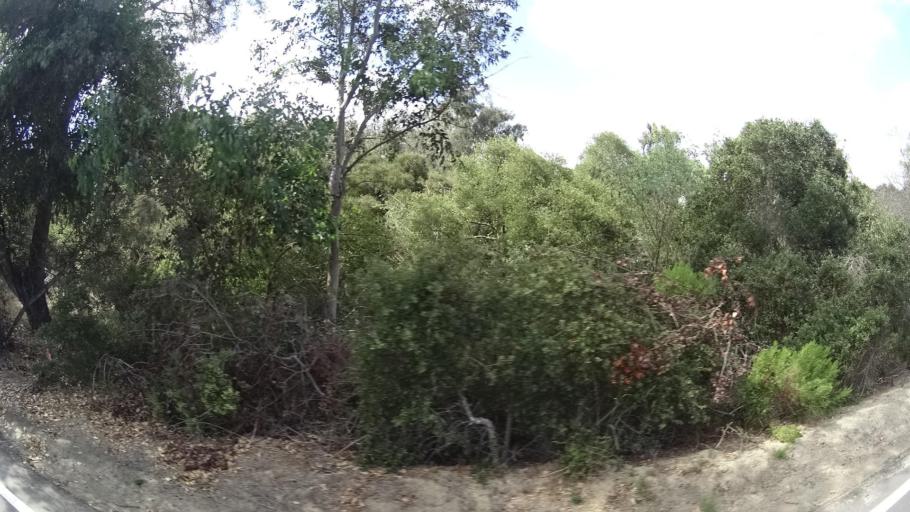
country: US
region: California
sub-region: San Diego County
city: Rancho Santa Fe
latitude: 33.0174
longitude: -117.2182
